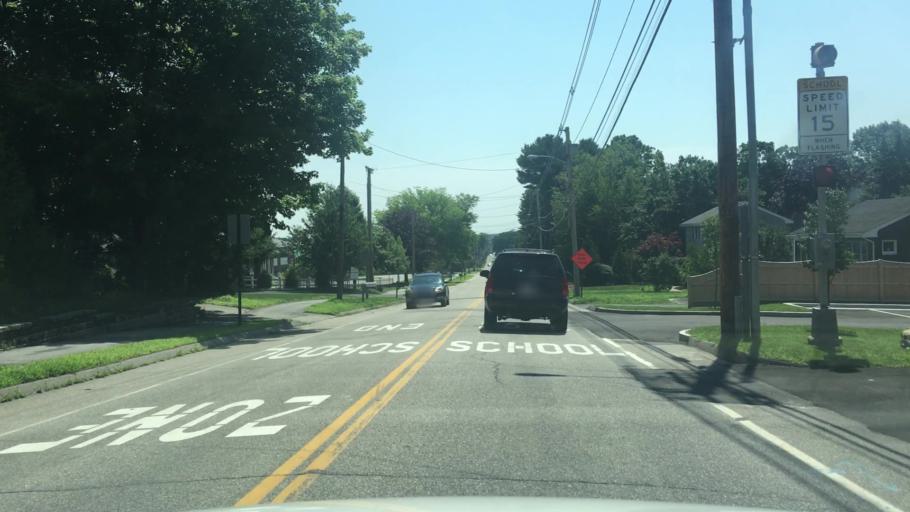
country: US
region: Maine
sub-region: Cumberland County
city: Cumberland Center
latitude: 43.7957
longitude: -70.2568
